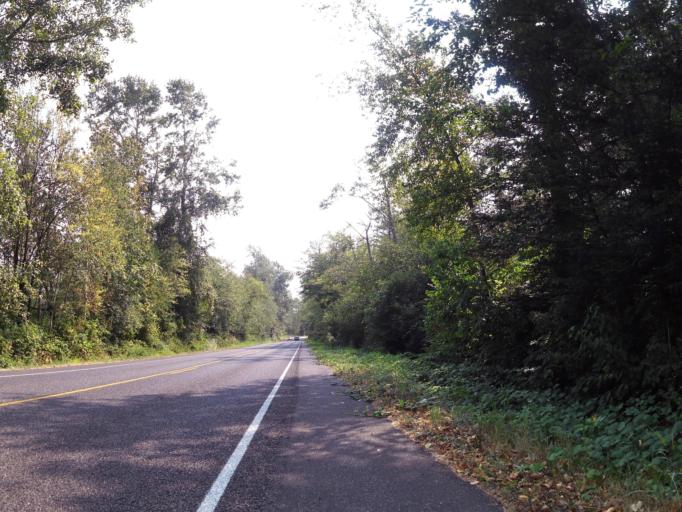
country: US
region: Washington
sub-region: Whatcom County
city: Marietta-Alderwood
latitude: 48.7882
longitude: -122.5583
